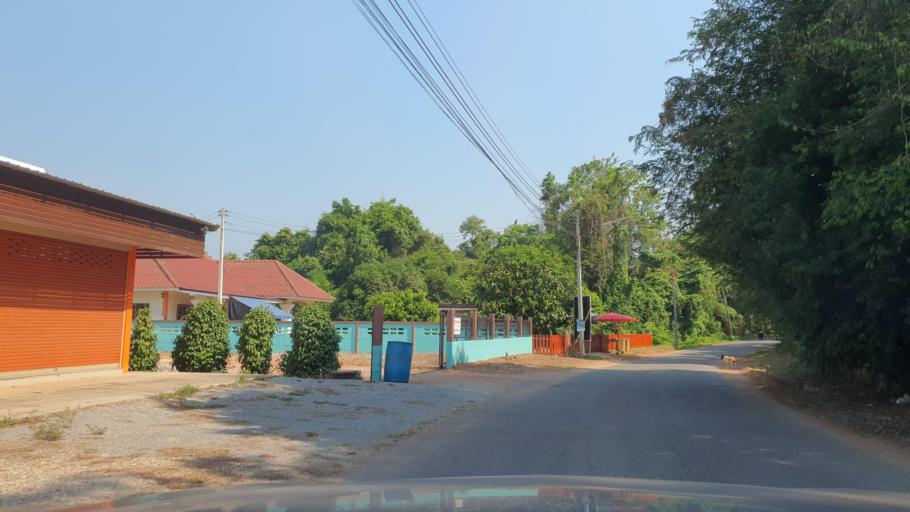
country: TH
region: Kanchanaburi
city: Kanchanaburi
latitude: 14.0701
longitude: 99.4847
